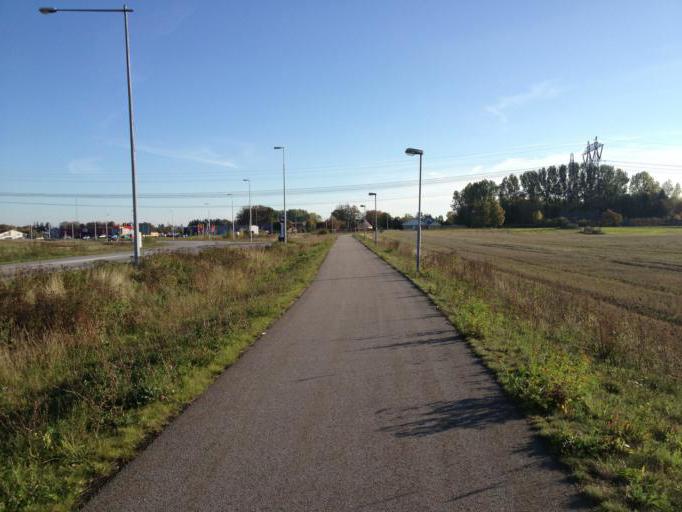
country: SE
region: Skane
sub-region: Kavlinge Kommun
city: Loddekopinge
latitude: 55.7429
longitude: 13.0297
